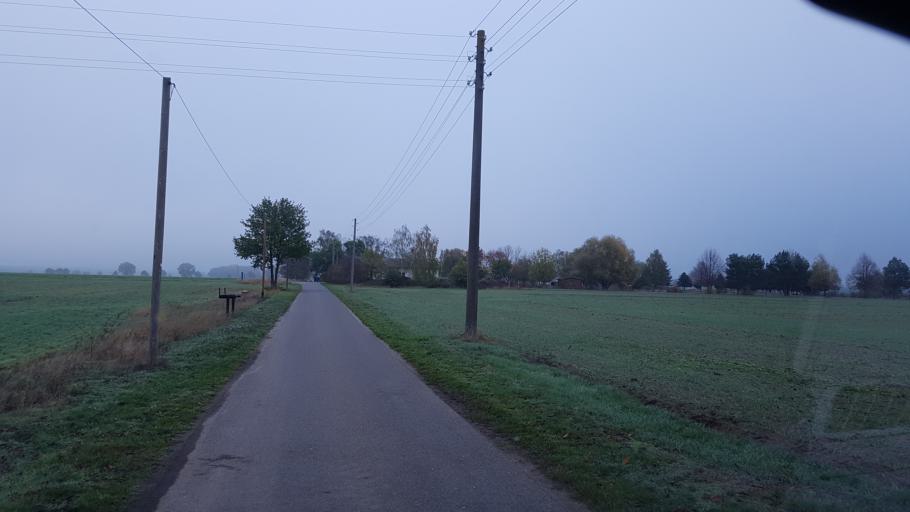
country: DE
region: Brandenburg
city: Sonnewalde
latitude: 51.6732
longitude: 13.6289
